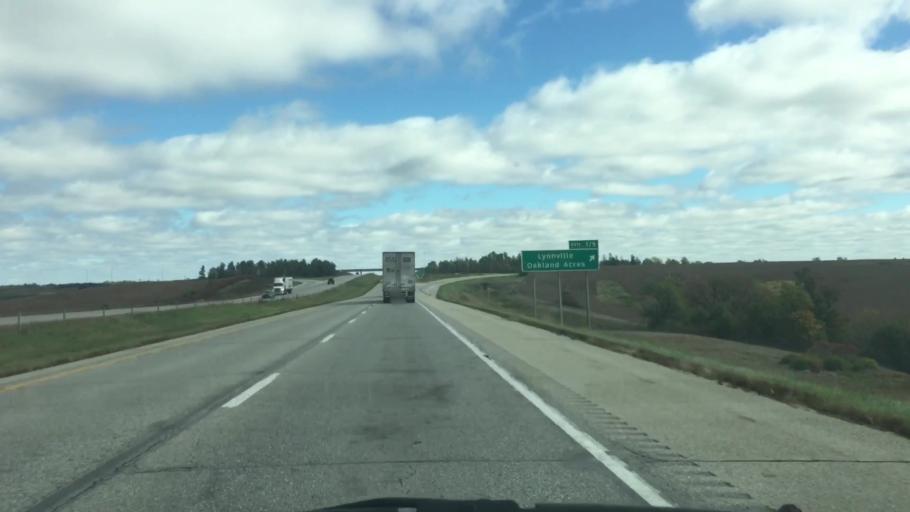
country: US
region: Iowa
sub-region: Poweshiek County
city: Grinnell
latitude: 41.6952
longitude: -92.8051
